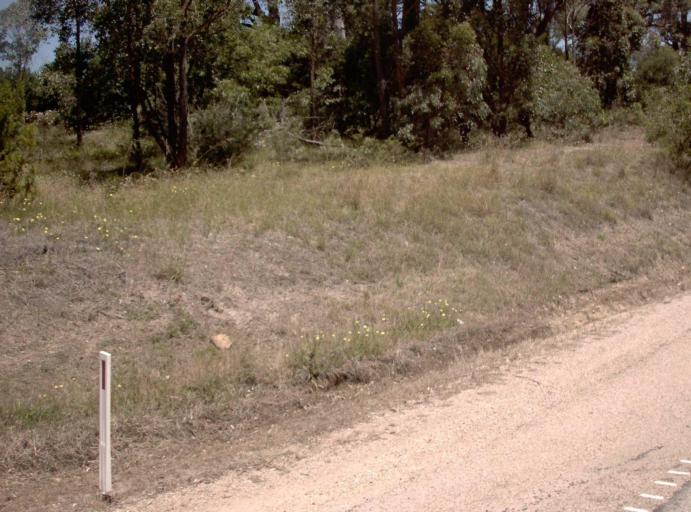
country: AU
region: Victoria
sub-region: East Gippsland
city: Bairnsdale
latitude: -37.7510
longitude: 147.7476
